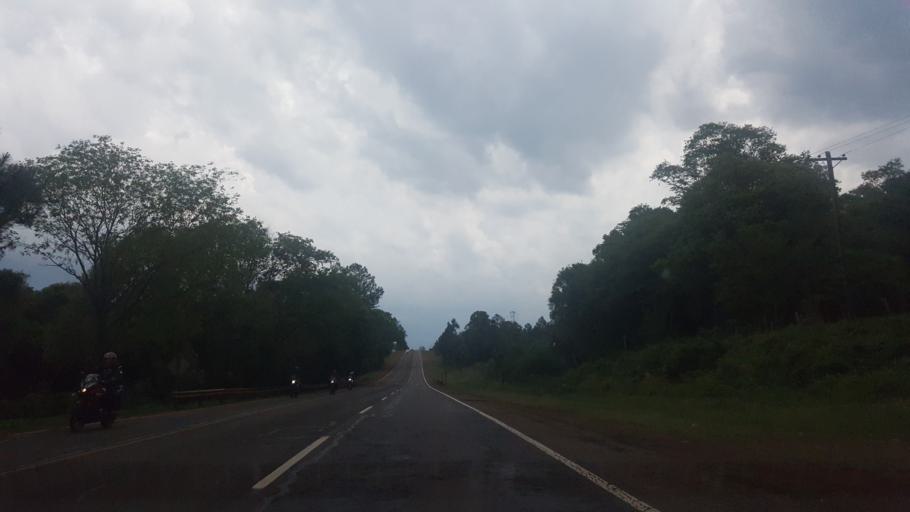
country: AR
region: Misiones
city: Santo Pipo
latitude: -27.1232
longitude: -55.3784
